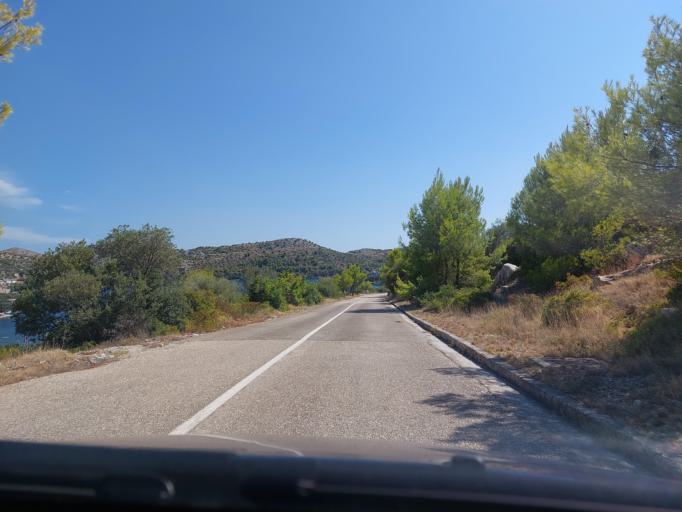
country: HR
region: Dubrovacko-Neretvanska
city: Smokvica
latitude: 42.7388
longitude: 16.8854
